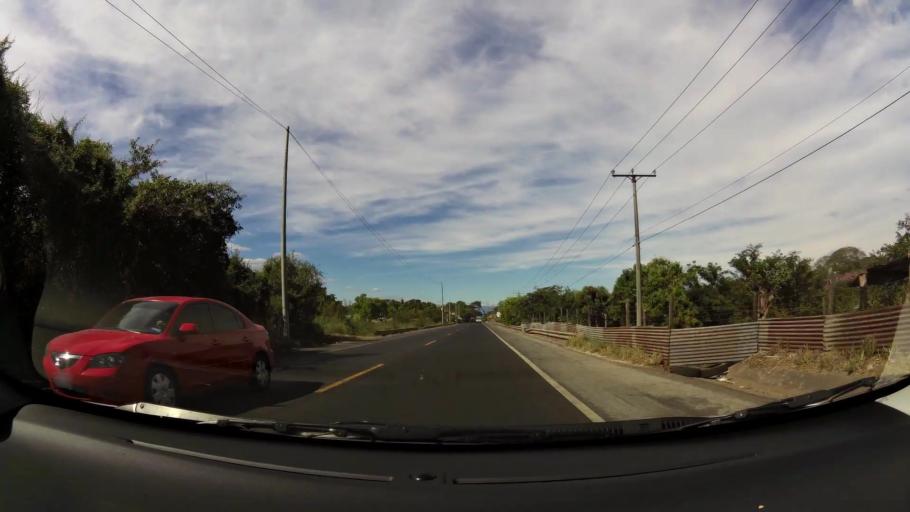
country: SV
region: San Salvador
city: Guazapa
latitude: 13.9094
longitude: -89.1813
